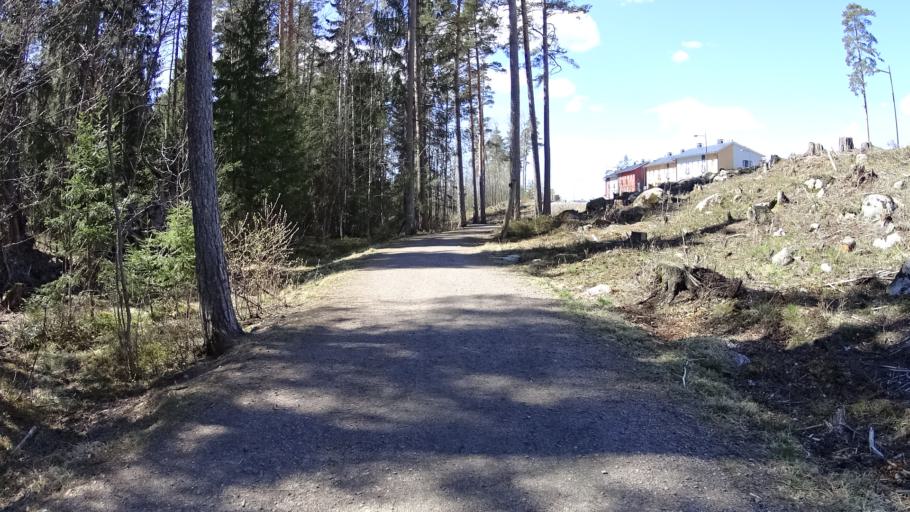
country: FI
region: Uusimaa
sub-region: Helsinki
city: Espoo
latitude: 60.1967
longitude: 24.6064
